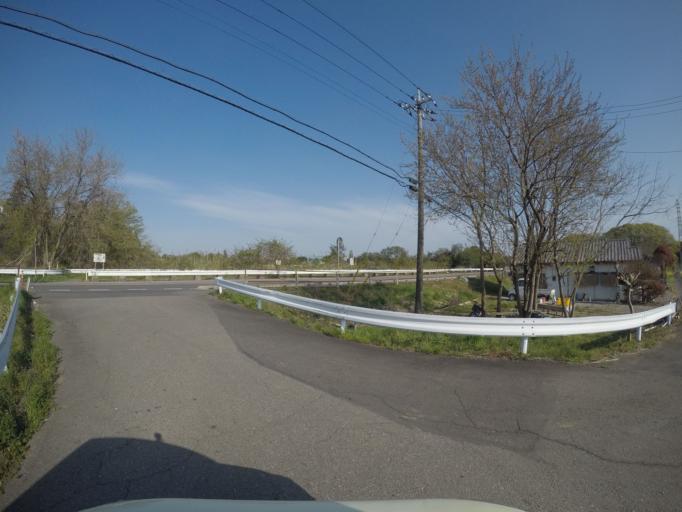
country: JP
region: Ibaraki
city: Ishige
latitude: 36.1809
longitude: 140.0176
